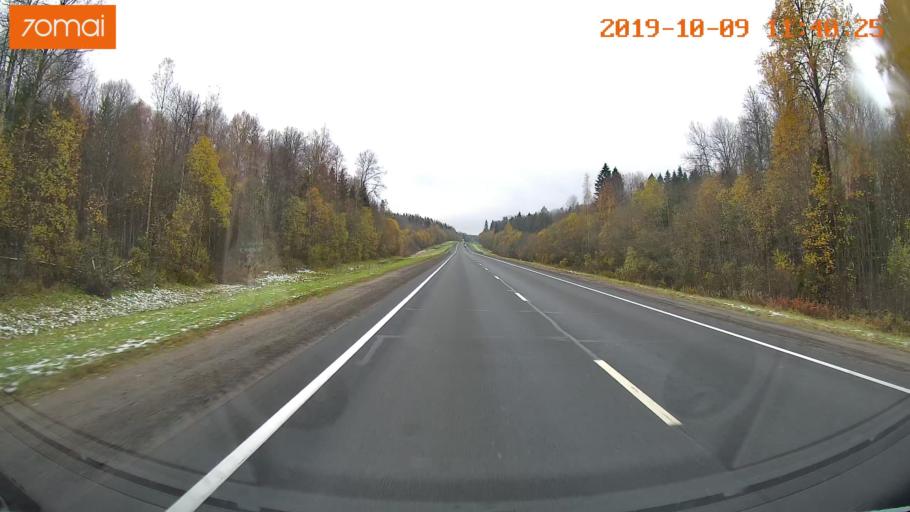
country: RU
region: Vologda
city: Gryazovets
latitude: 58.9427
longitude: 40.1740
